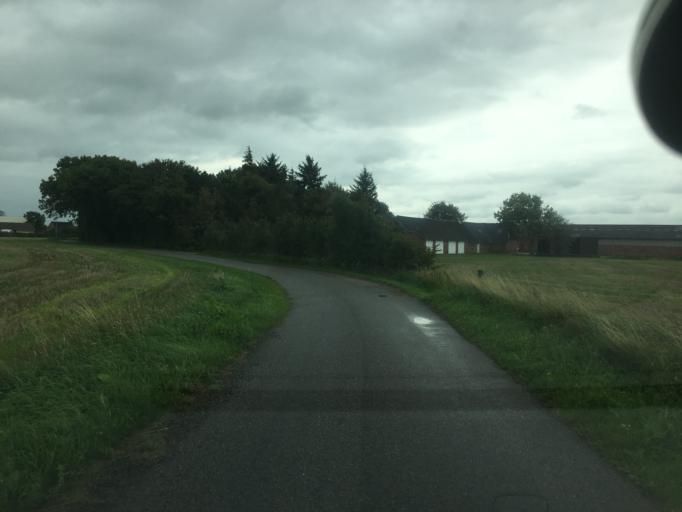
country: DK
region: South Denmark
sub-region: Tonder Kommune
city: Tonder
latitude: 54.9637
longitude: 8.9281
